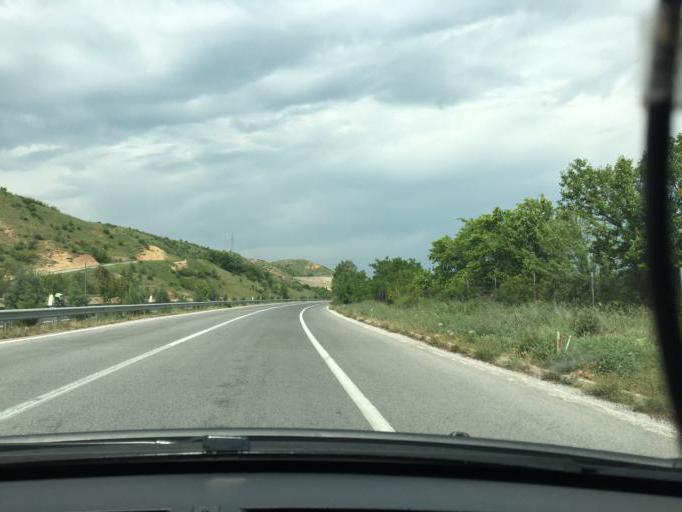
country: MK
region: Demir Kapija
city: Demir Kapija
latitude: 41.4280
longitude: 22.1848
